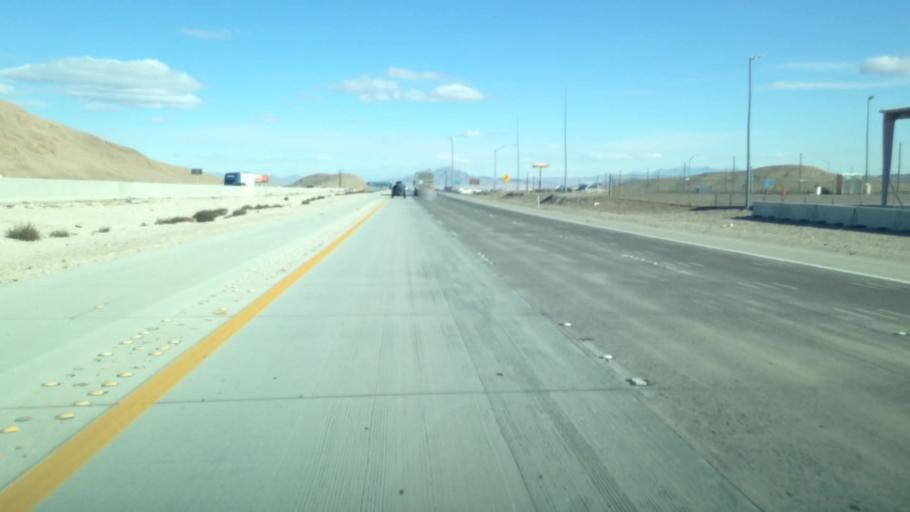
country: US
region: Nevada
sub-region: Clark County
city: Enterprise
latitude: 35.9272
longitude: -115.1953
